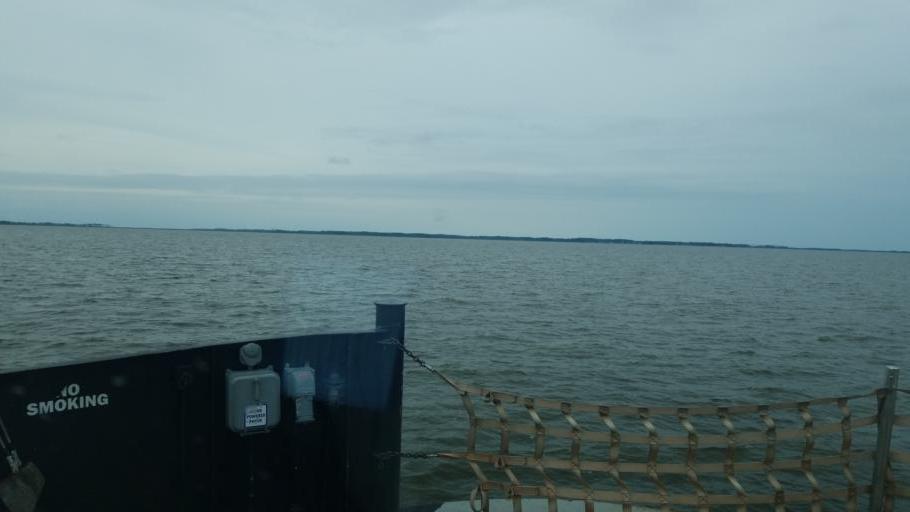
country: US
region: North Carolina
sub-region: Currituck County
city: Currituck
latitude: 36.4604
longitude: -75.9747
